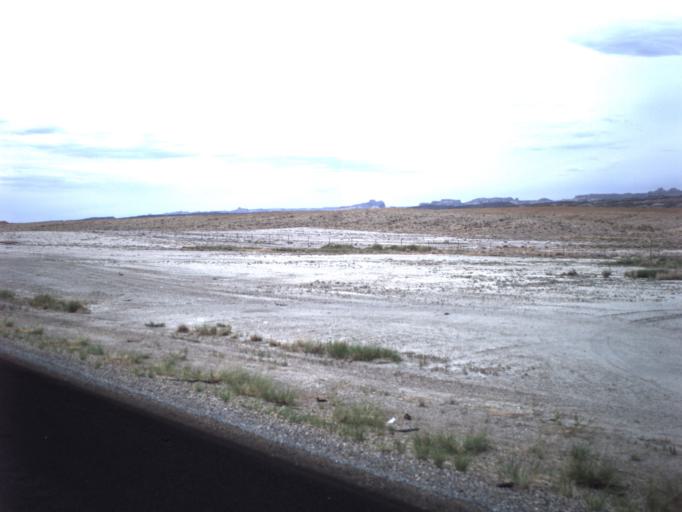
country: US
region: Utah
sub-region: Carbon County
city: East Carbon City
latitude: 39.1545
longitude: -110.3380
